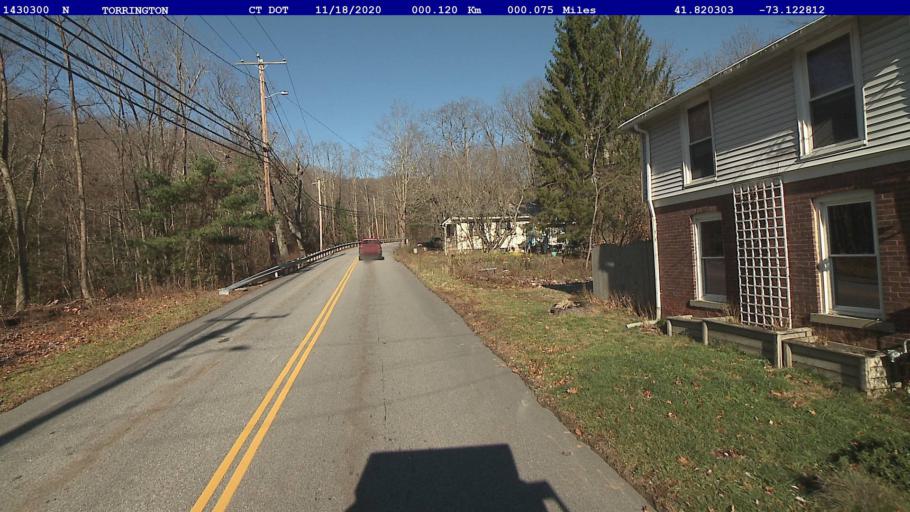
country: US
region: Connecticut
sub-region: Litchfield County
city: Torrington
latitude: 41.8203
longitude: -73.1228
